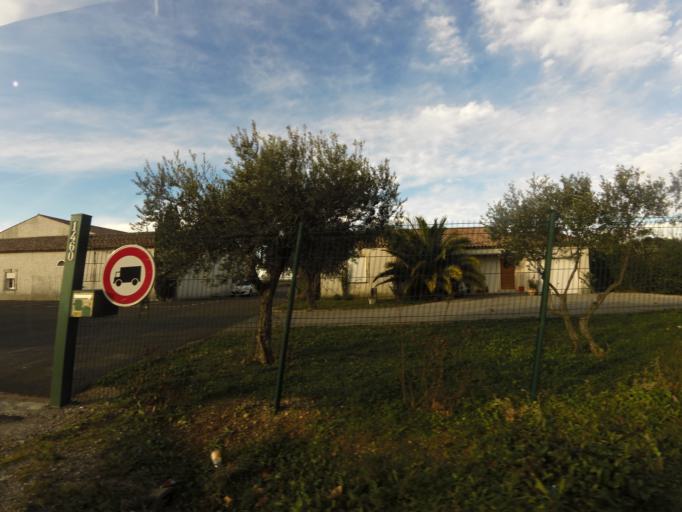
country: FR
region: Languedoc-Roussillon
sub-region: Departement du Gard
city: Mus
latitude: 43.7135
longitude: 4.1977
